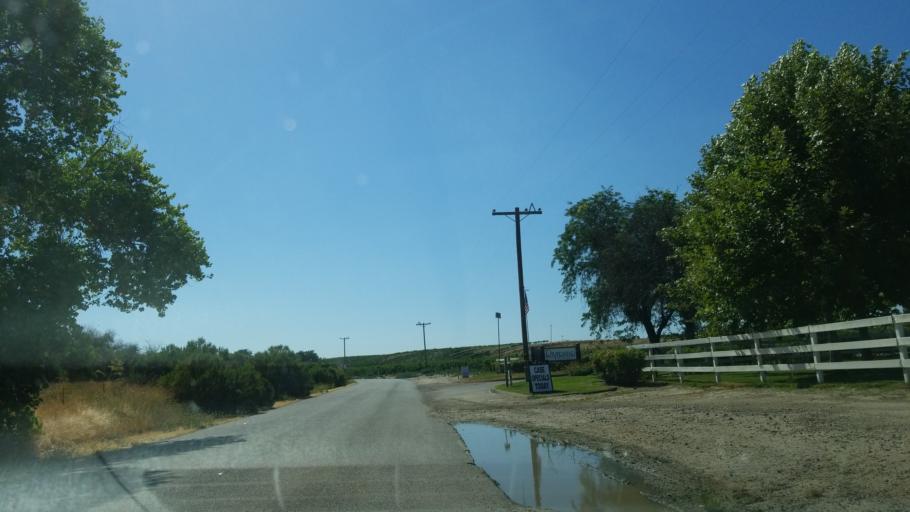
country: US
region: California
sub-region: San Luis Obispo County
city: San Miguel
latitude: 35.7185
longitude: -120.6422
